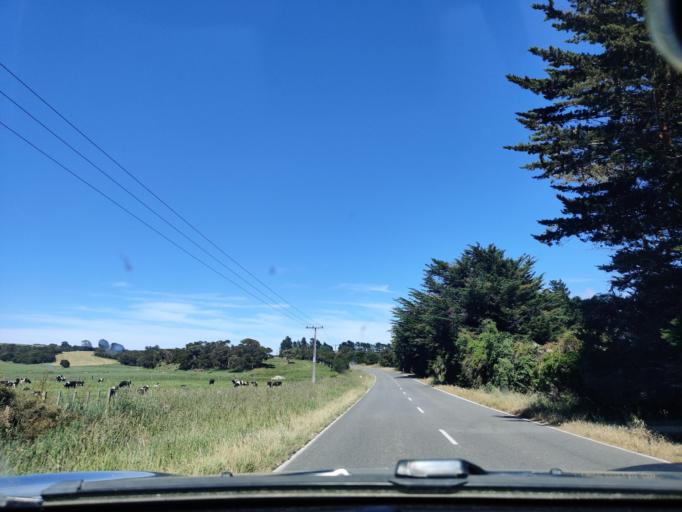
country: NZ
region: Wellington
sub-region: Upper Hutt City
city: Upper Hutt
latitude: -41.3206
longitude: 175.2517
